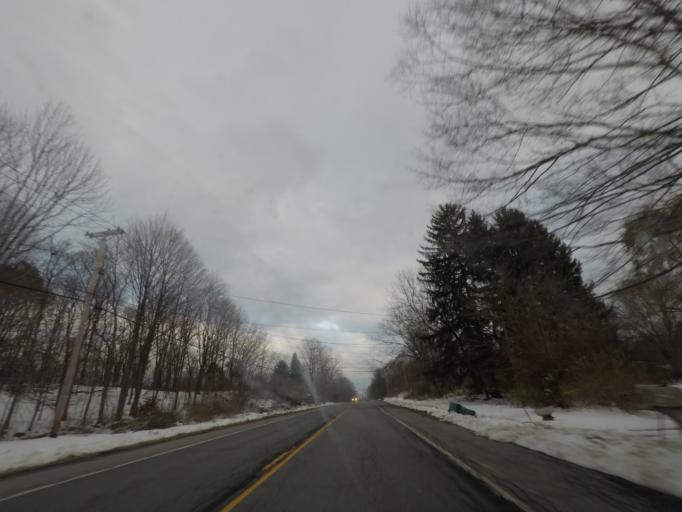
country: US
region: New York
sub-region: Ulster County
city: Plattekill
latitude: 41.6242
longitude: -74.0867
